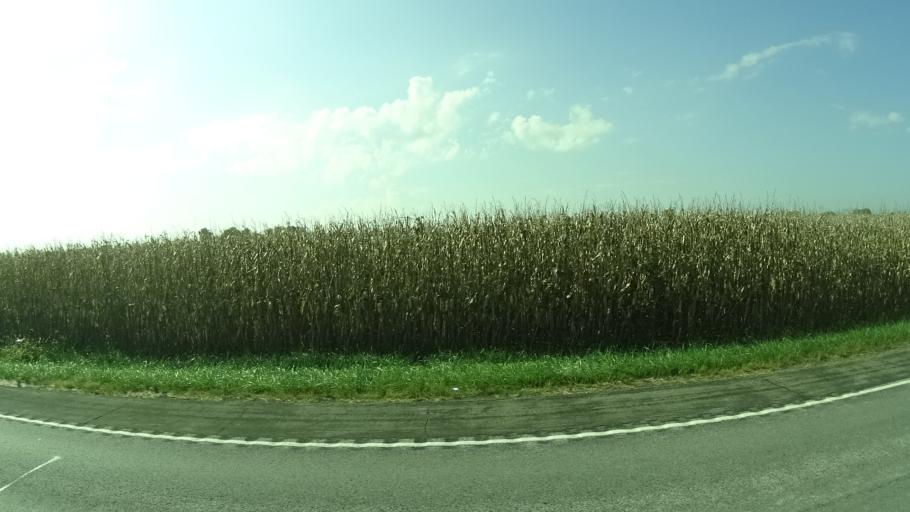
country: US
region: Indiana
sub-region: Madison County
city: Lapel
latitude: 40.0224
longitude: -85.8588
